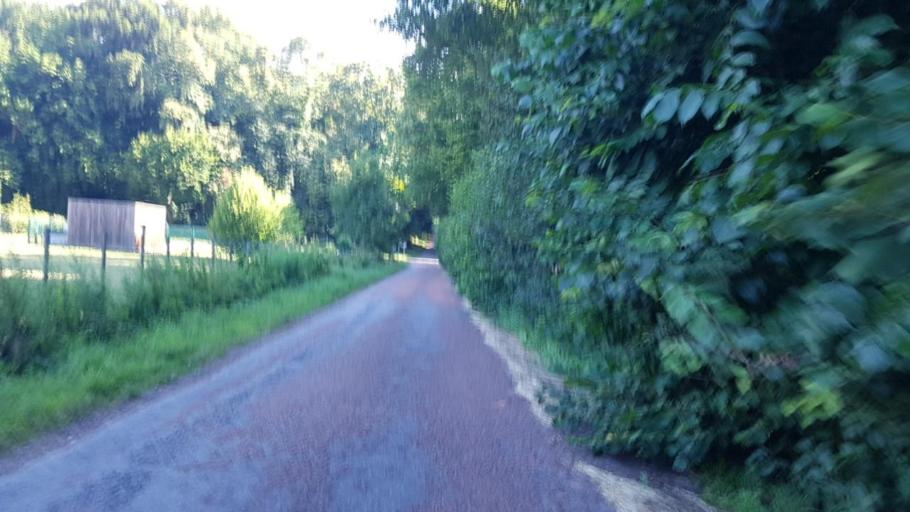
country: FR
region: Picardie
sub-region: Departement de l'Oise
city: Chamant
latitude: 49.2505
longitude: 2.6152
